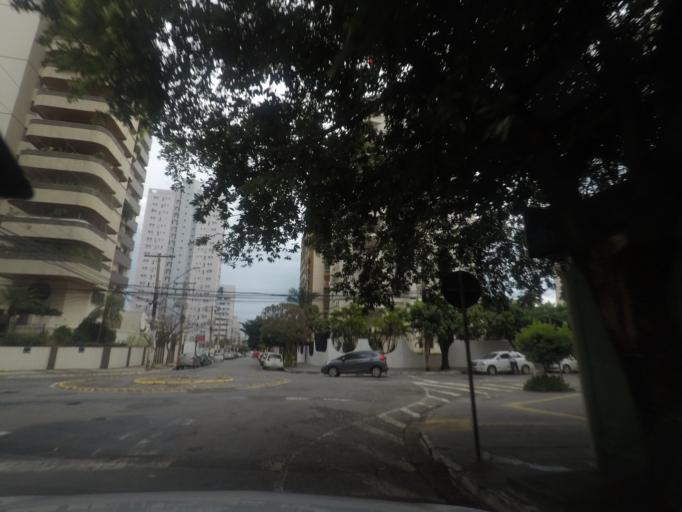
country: BR
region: Goias
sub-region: Goiania
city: Goiania
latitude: -16.6809
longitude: -49.2677
